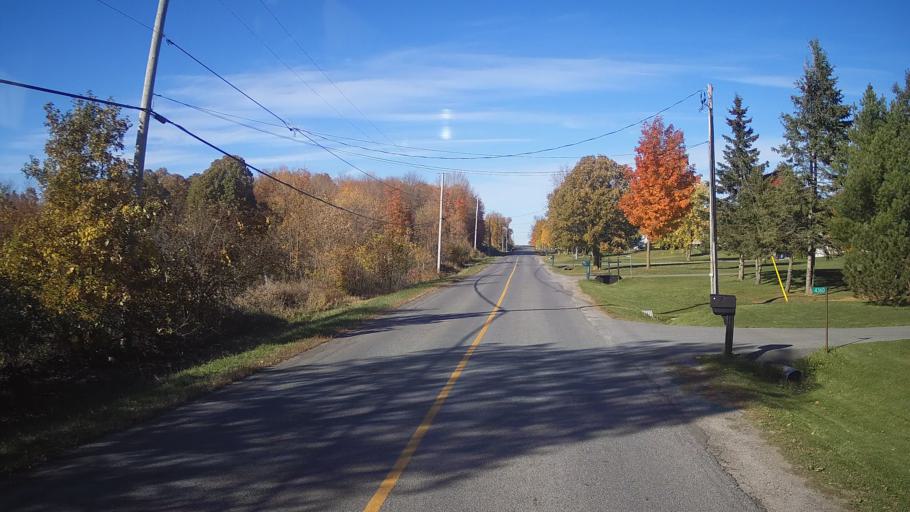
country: CA
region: Ontario
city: Kingston
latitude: 44.4117
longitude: -76.5275
